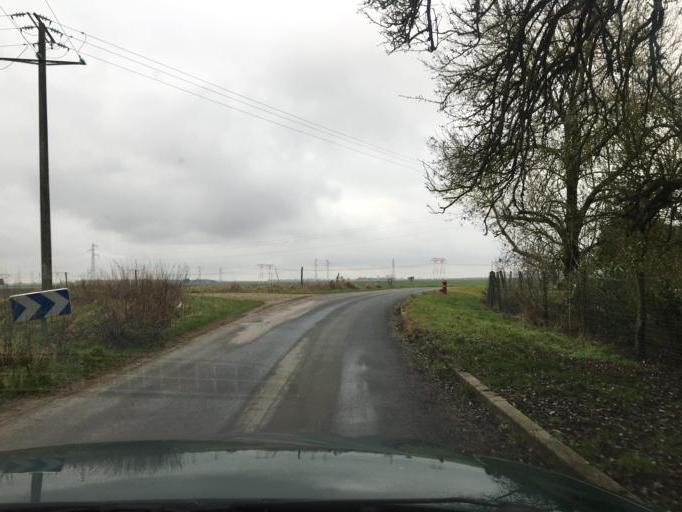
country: FR
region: Centre
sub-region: Departement du Loiret
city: Gidy
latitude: 48.0181
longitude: 1.8346
